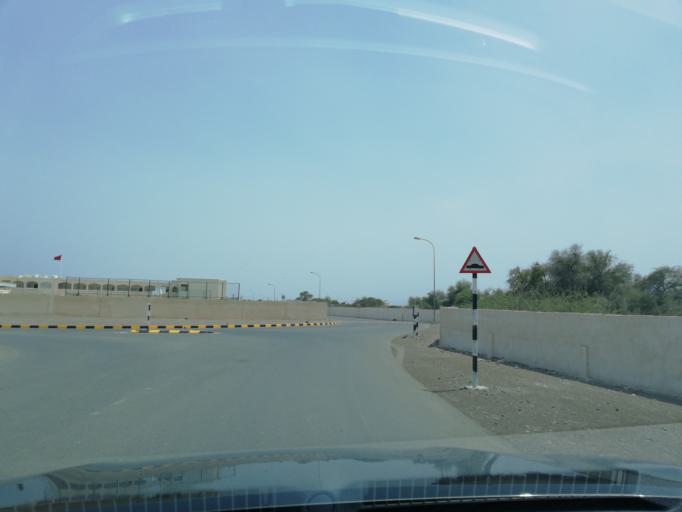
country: OM
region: Al Batinah
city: Shinas
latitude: 24.7385
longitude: 56.4678
